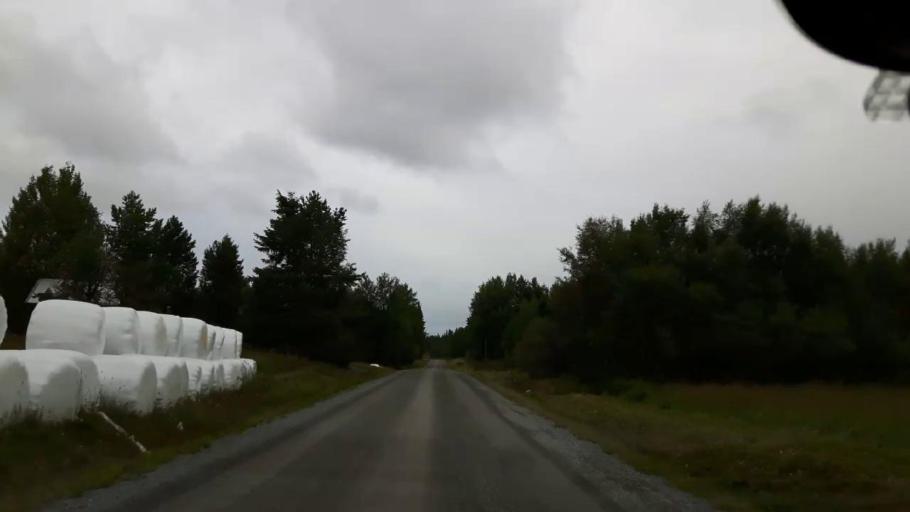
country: SE
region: Jaemtland
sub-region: OEstersunds Kommun
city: Ostersund
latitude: 63.1084
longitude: 14.5457
